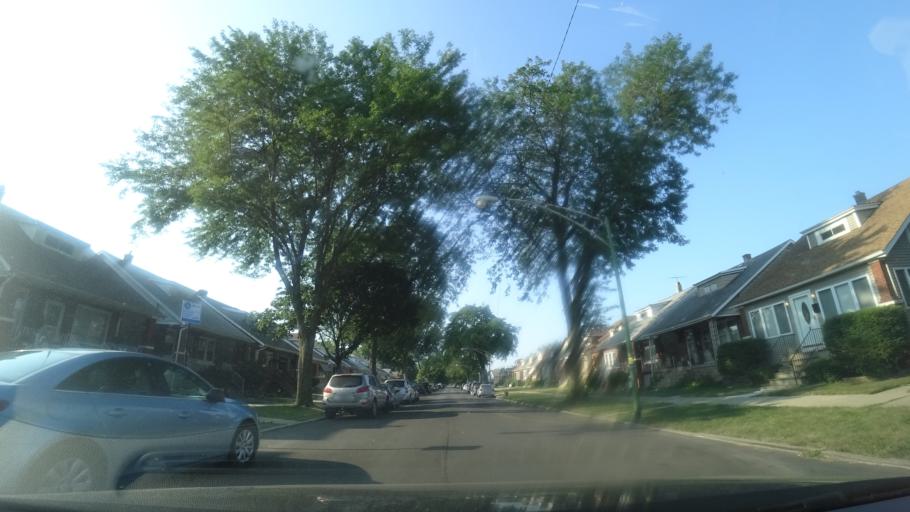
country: US
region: Illinois
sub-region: Cook County
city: Elmwood Park
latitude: 41.9290
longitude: -87.7698
